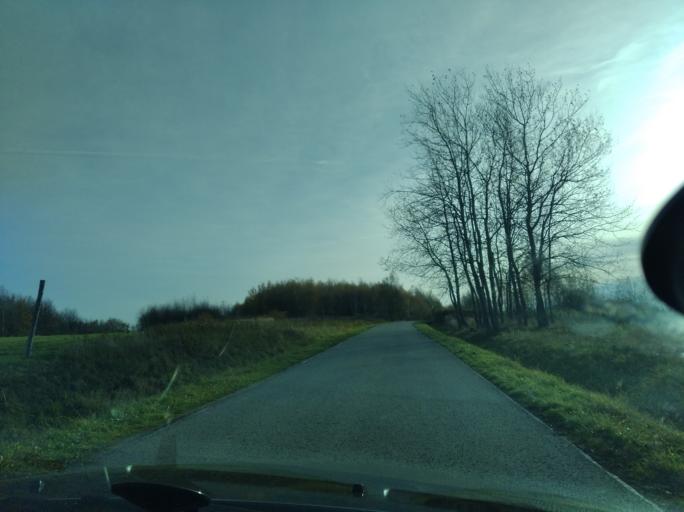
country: PL
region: Subcarpathian Voivodeship
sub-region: Powiat rzeszowski
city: Siedliska
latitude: 49.9365
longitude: 21.9555
